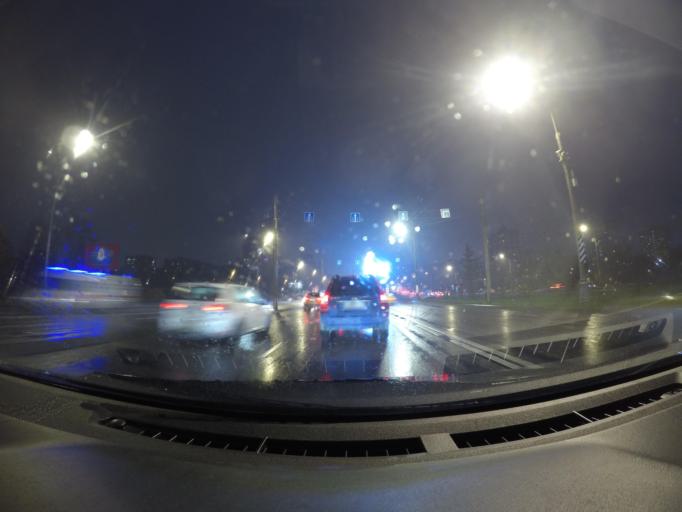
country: RU
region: Moskovskaya
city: Kozhukhovo
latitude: 55.7002
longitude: 37.6674
